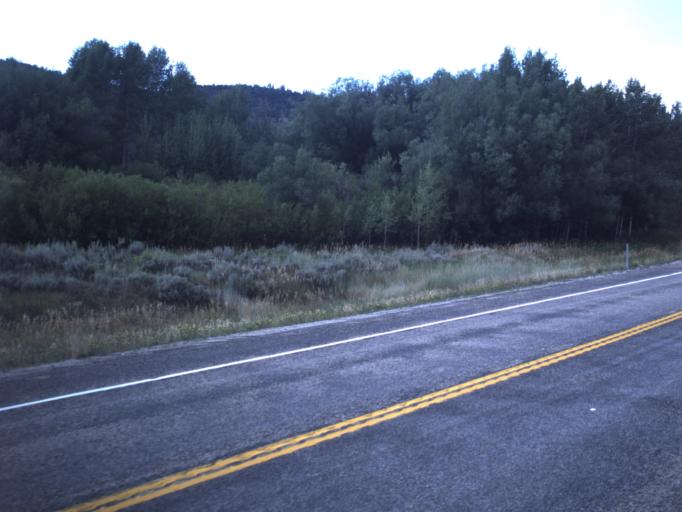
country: US
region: Utah
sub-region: Cache County
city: Richmond
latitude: 41.8822
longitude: -111.5629
